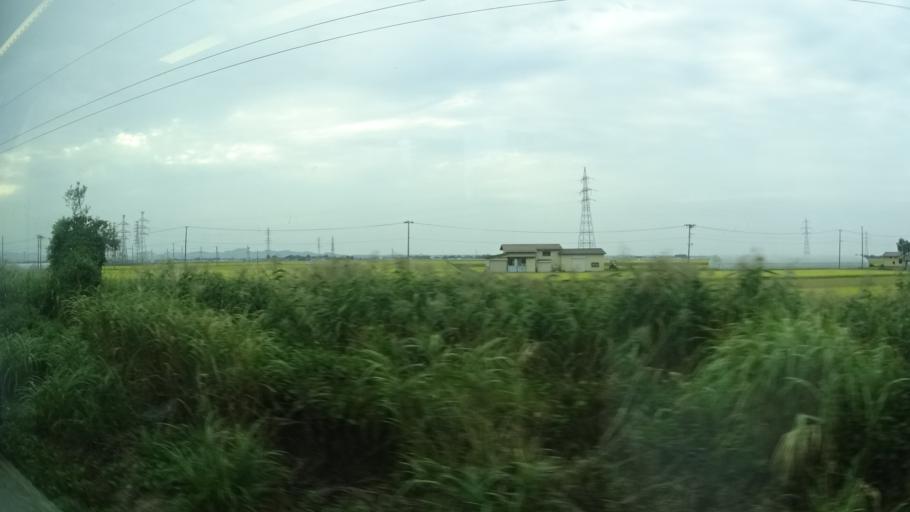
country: JP
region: Yamagata
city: Tsuruoka
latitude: 38.7672
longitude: 139.8924
